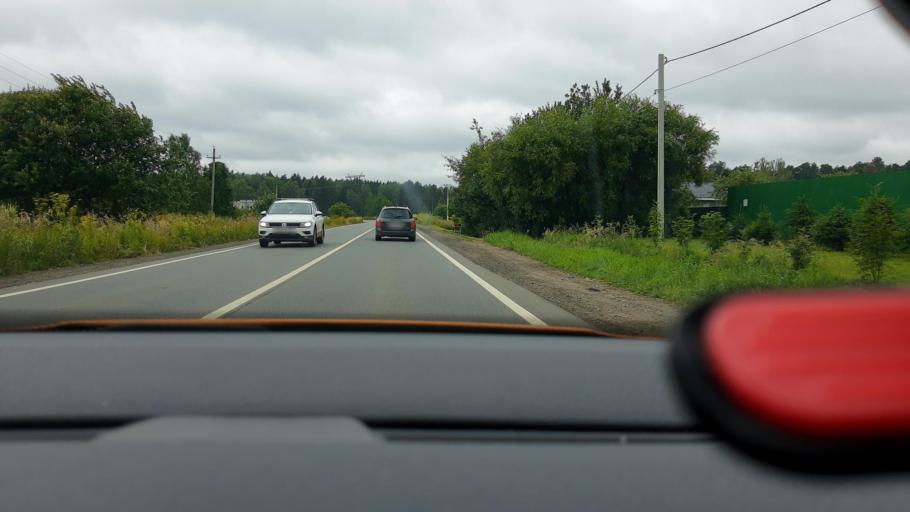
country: RU
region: Moskovskaya
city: Pirogovskiy
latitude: 55.9987
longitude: 37.7057
